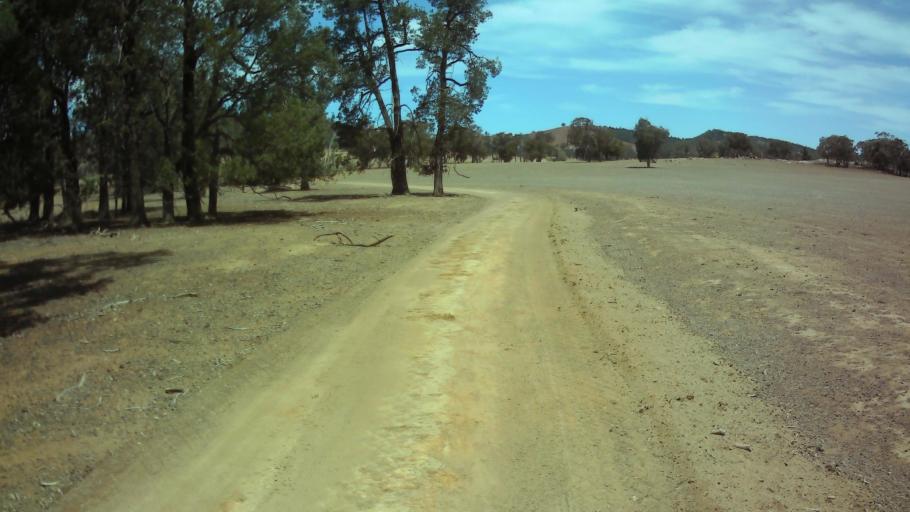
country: AU
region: New South Wales
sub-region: Weddin
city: Grenfell
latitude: -33.7722
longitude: 148.1513
